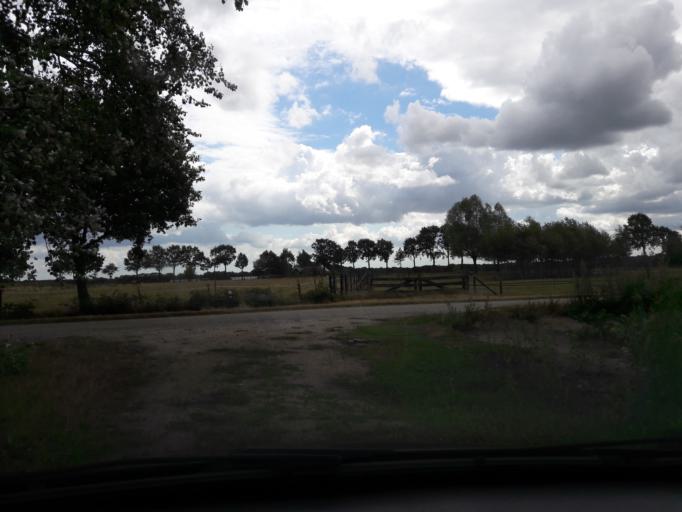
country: NL
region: Drenthe
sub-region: Gemeente Borger-Odoorn
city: Borger
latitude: 52.9542
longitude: 6.8099
